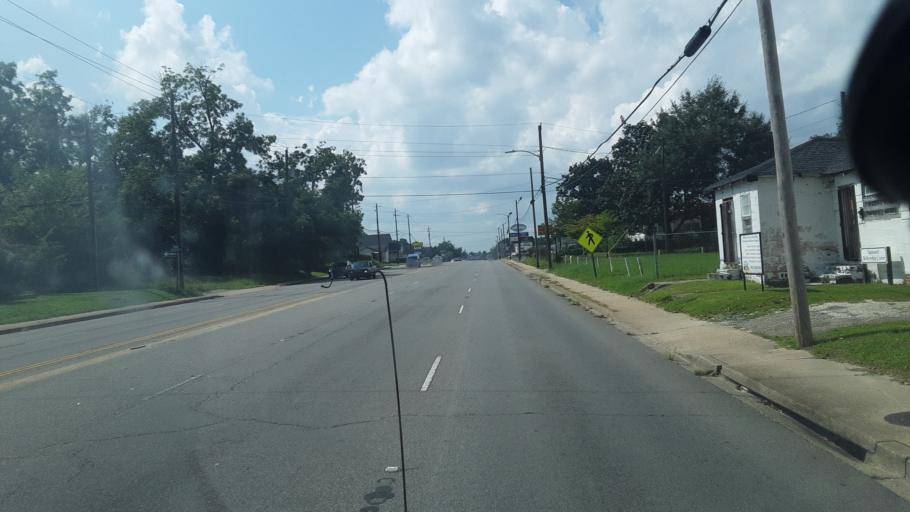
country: US
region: South Carolina
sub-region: Sumter County
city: Sumter
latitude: 33.9402
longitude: -80.3645
